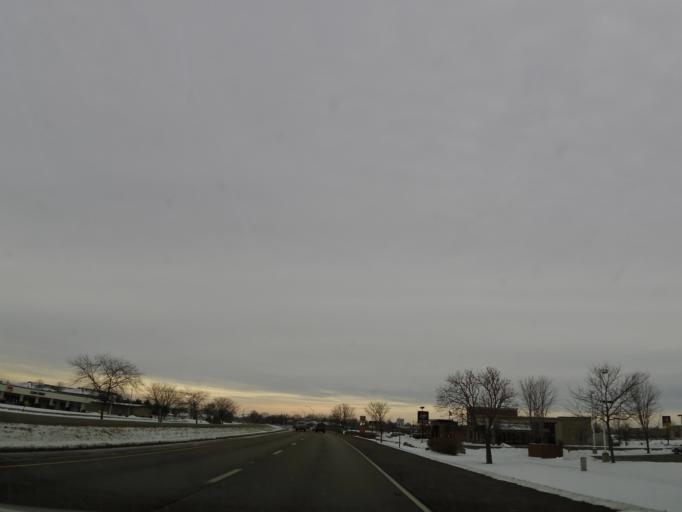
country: US
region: Illinois
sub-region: LaSalle County
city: Peru
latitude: 41.3513
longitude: -89.1253
